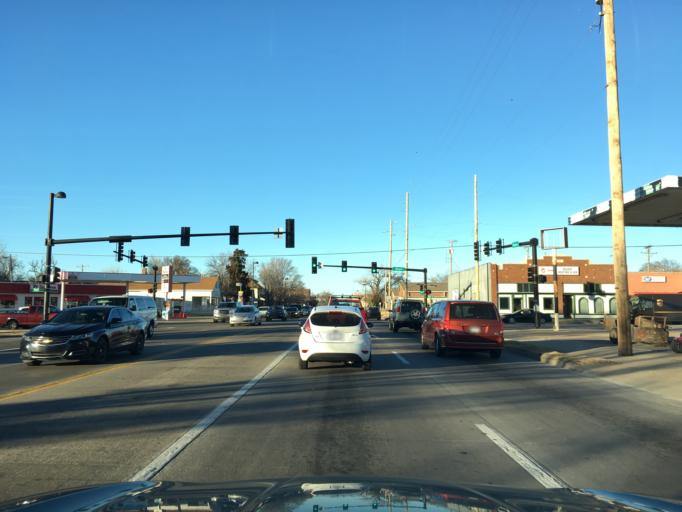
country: US
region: Kansas
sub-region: Sedgwick County
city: Wichita
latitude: 37.6800
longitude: -97.3530
